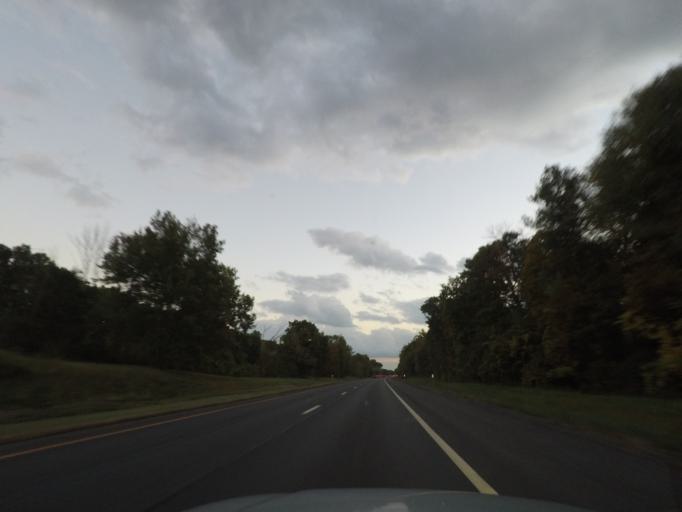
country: US
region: New York
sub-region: Ulster County
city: New Paltz
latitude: 41.7721
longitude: -74.0528
